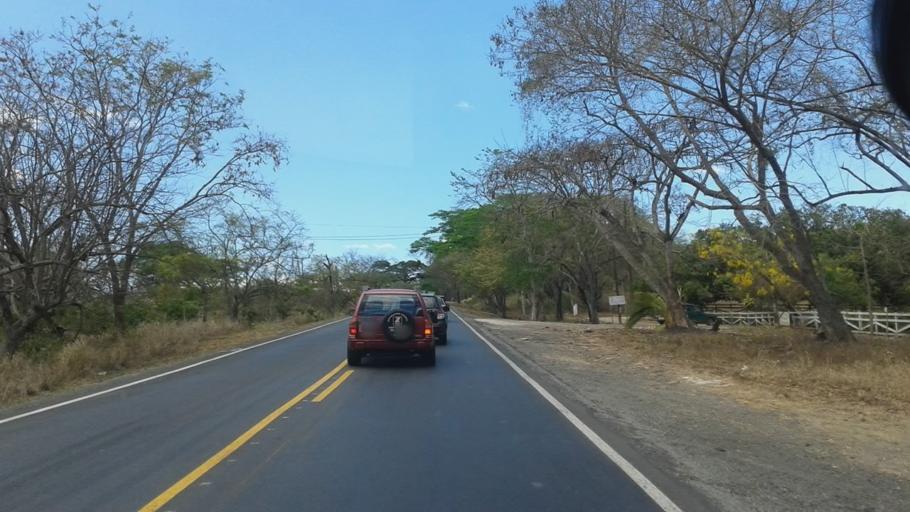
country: CR
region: Guanacaste
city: Juntas
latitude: 10.1380
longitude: -84.9061
